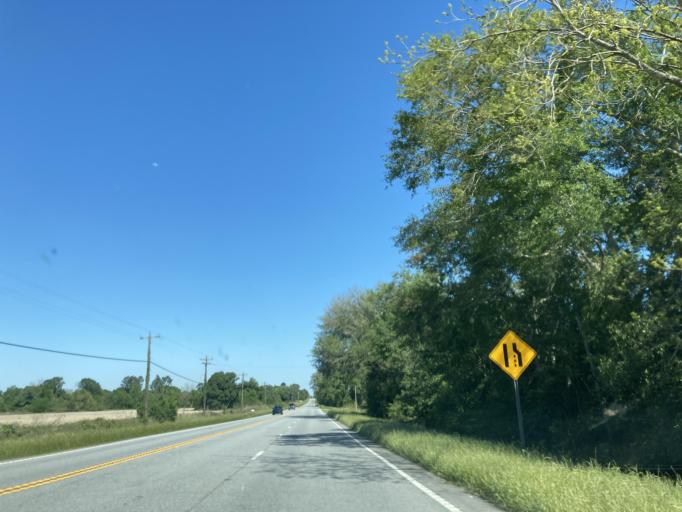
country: US
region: Georgia
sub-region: Miller County
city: Colquitt
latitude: 31.1848
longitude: -84.5868
